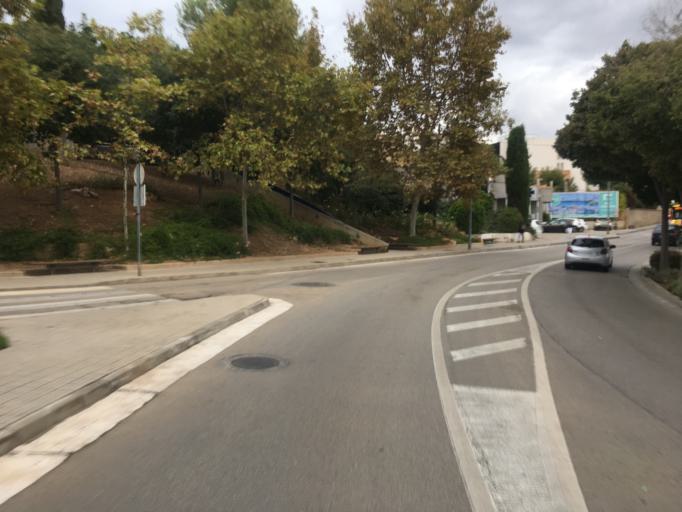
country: ES
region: Balearic Islands
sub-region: Illes Balears
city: Palma
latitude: 39.5470
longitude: 2.5951
